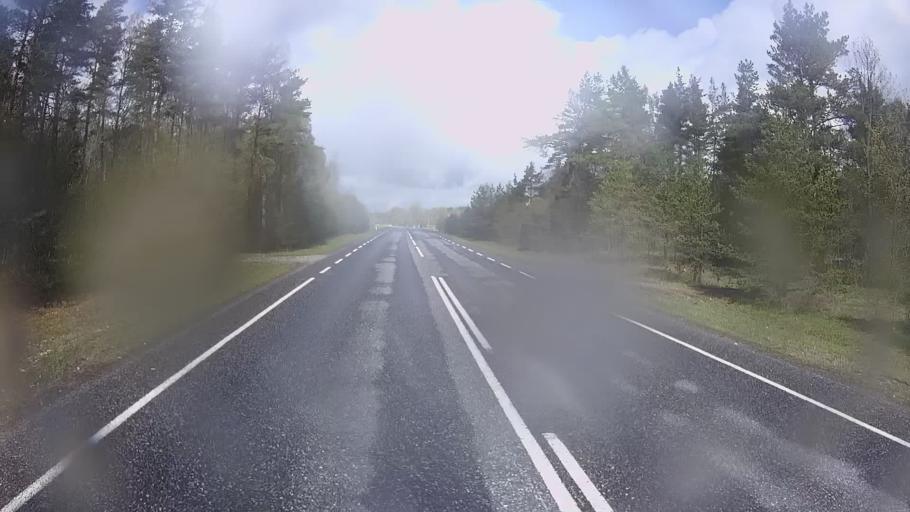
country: EE
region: Hiiumaa
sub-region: Kaerdla linn
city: Kardla
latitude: 58.8726
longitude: 22.9613
